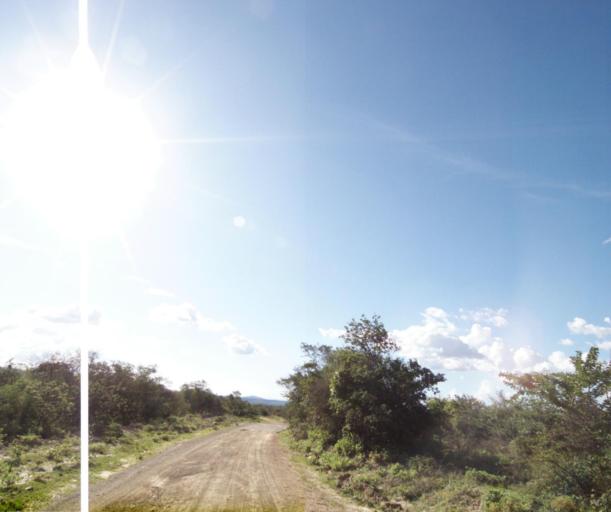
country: BR
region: Bahia
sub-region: Tanhacu
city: Tanhacu
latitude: -14.1894
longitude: -40.9736
